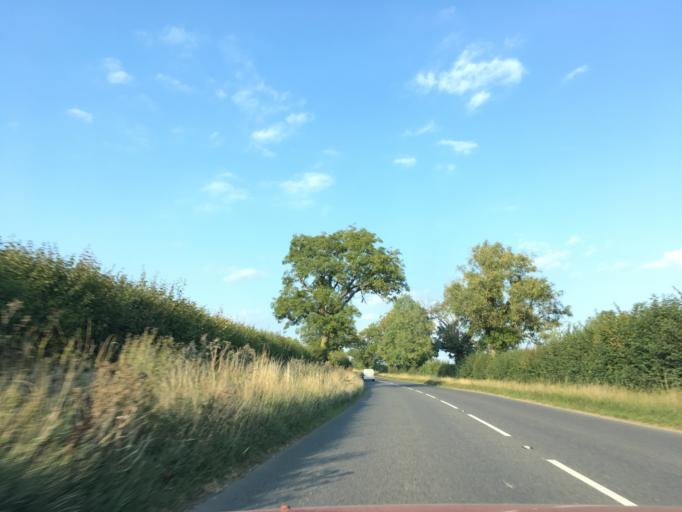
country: GB
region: England
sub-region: Gloucestershire
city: Stow on the Wold
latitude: 51.9121
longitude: -1.7313
